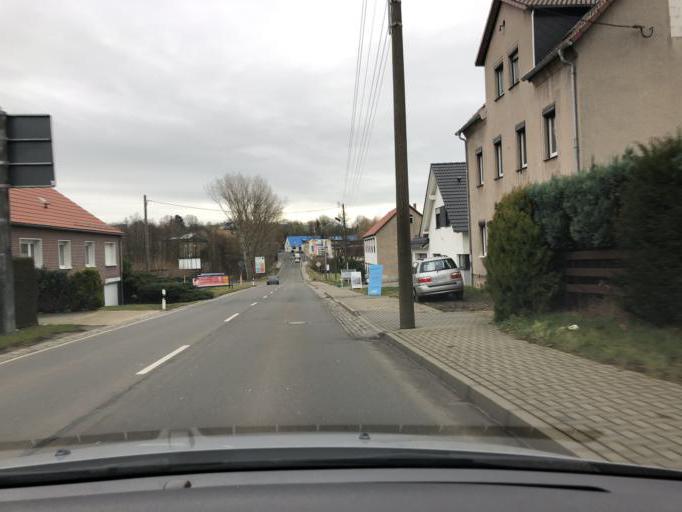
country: DE
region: Saxony
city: Dobeln
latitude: 51.1373
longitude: 13.0983
